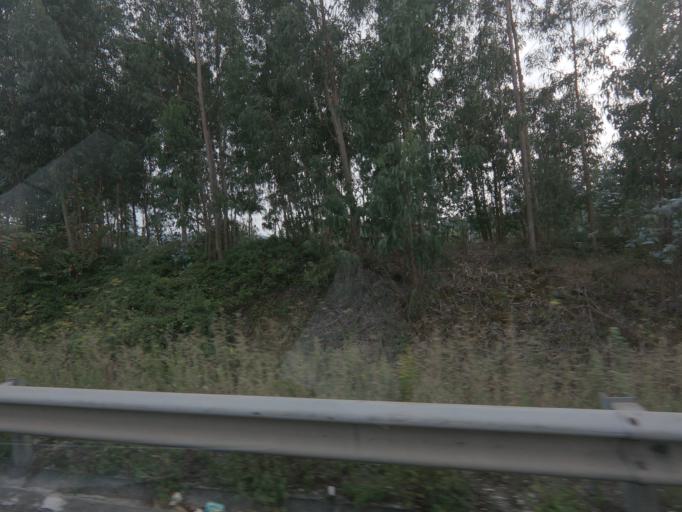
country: PT
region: Aveiro
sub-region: Mealhada
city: Pampilhosa do Botao
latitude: 40.3085
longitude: -8.3734
